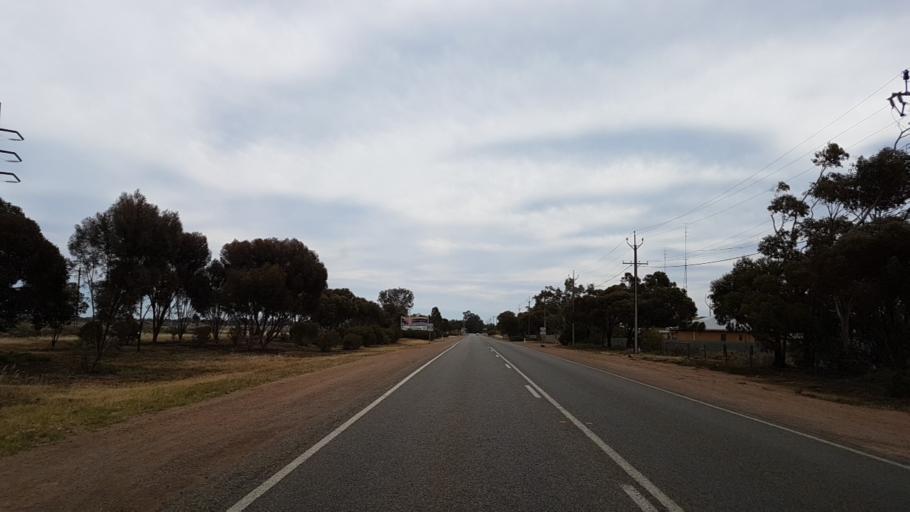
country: AU
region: South Australia
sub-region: Port Pirie City and Dists
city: Solomontown
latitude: -33.1928
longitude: 138.0419
